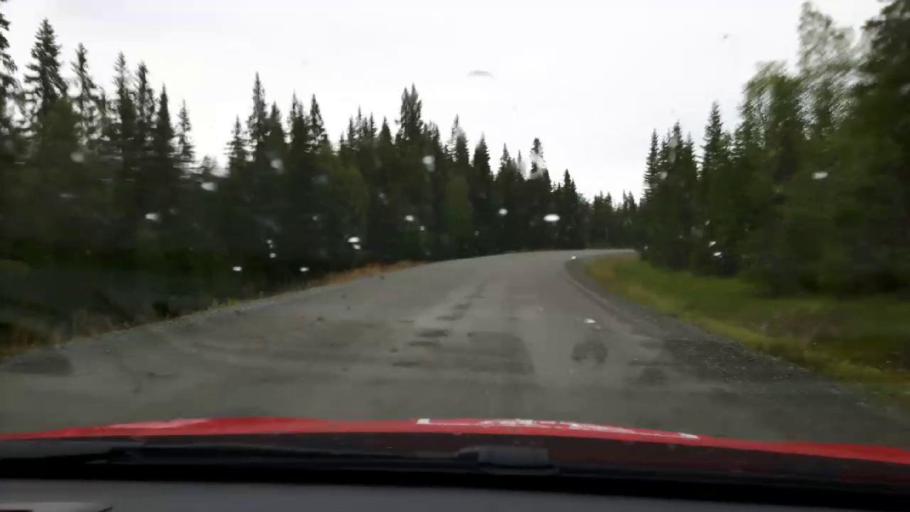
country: SE
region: Jaemtland
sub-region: Are Kommun
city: Are
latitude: 63.4211
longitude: 12.7513
